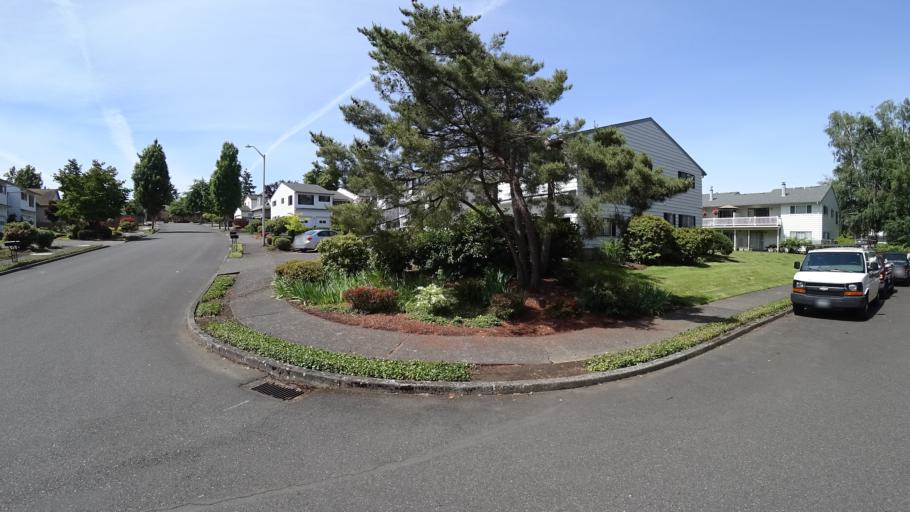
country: US
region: Oregon
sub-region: Multnomah County
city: Fairview
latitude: 45.5444
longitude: -122.5066
